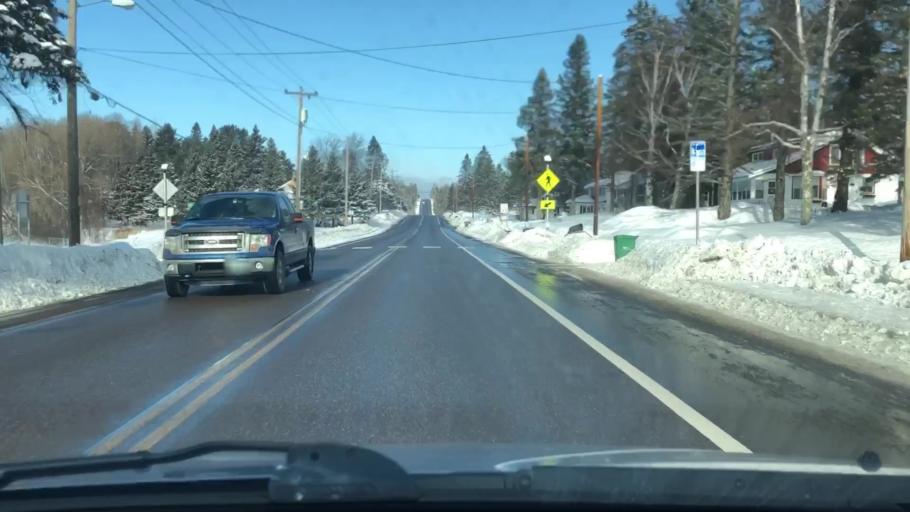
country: US
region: Minnesota
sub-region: Saint Louis County
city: Duluth
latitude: 46.8037
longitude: -92.1322
